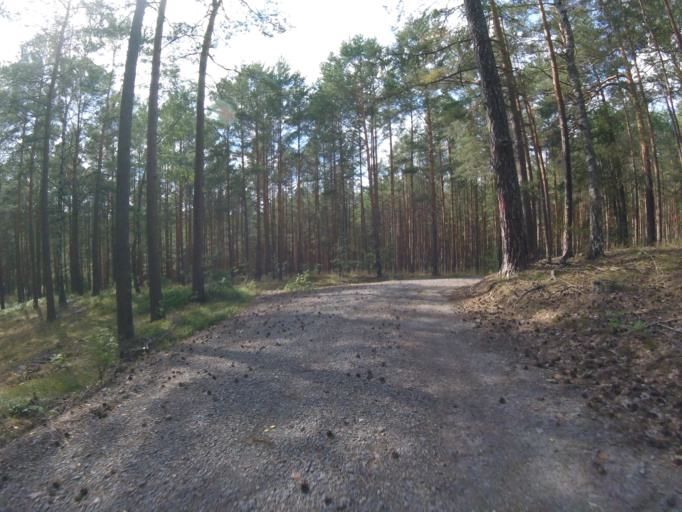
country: DE
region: Brandenburg
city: Halbe
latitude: 52.0650
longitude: 13.7827
